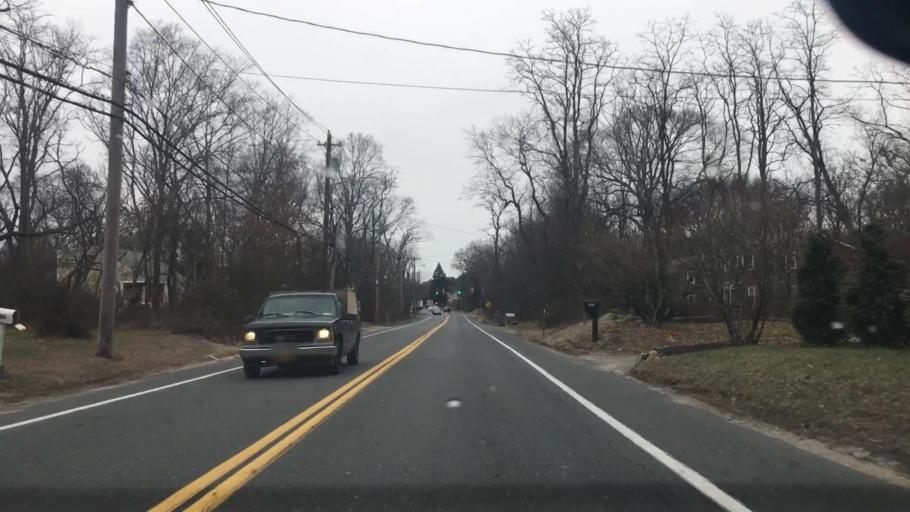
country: US
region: New York
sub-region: Suffolk County
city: Yaphank
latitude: 40.8556
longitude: -72.9383
